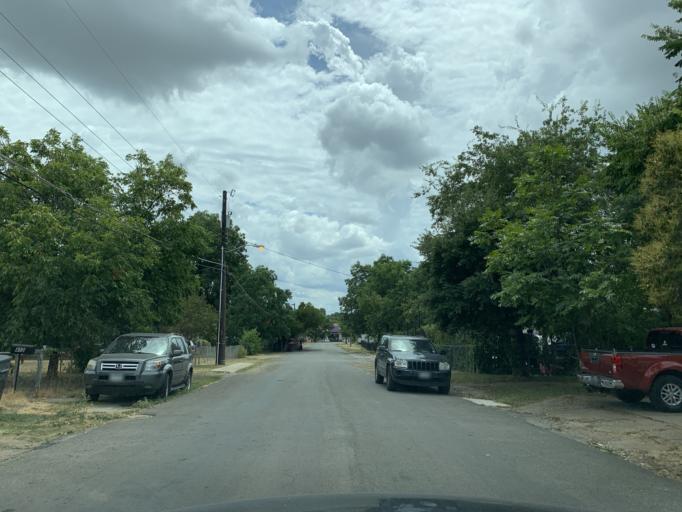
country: US
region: Texas
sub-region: Dallas County
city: Cockrell Hill
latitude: 32.7419
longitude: -96.8796
